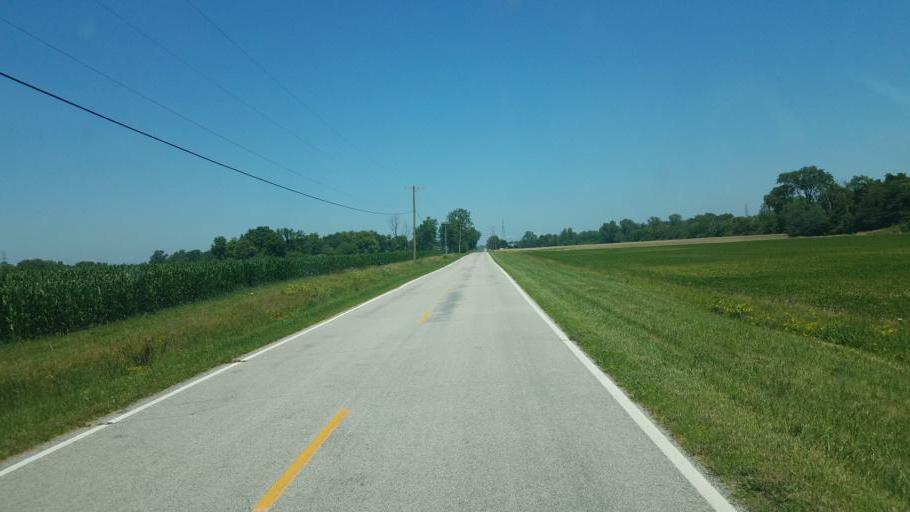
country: US
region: Ohio
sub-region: Sandusky County
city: Clyde
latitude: 41.3987
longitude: -83.0118
